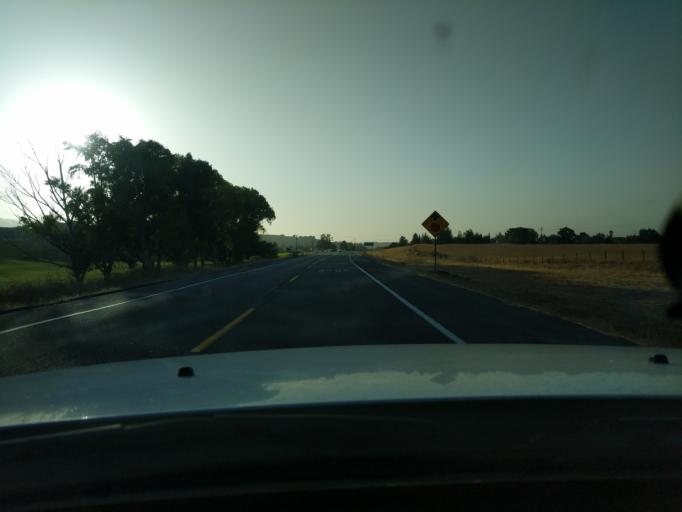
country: US
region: California
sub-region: San Benito County
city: Ridgemark
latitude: 36.8156
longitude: -121.3598
